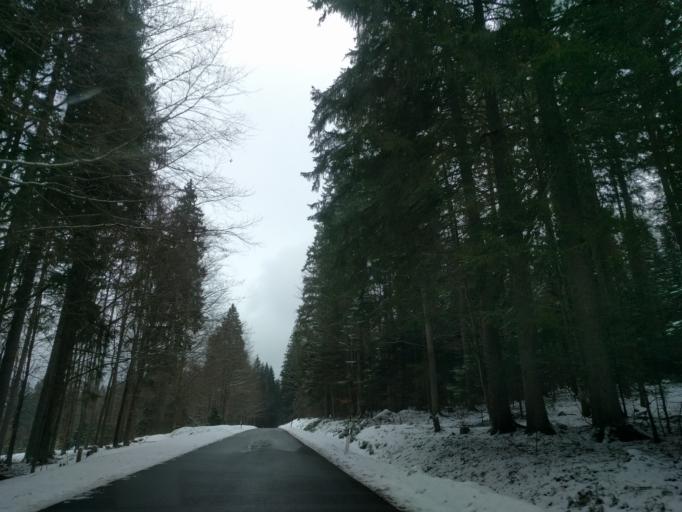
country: DE
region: Bavaria
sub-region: Lower Bavaria
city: Lindberg
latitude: 49.0549
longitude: 13.2958
